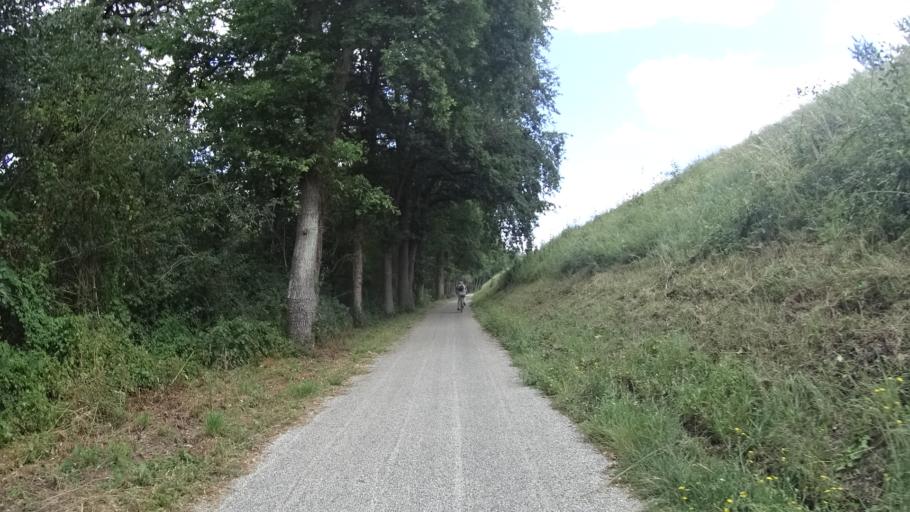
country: FR
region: Centre
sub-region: Departement d'Indre-et-Loire
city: Vouvray
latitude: 47.4029
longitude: 0.7860
